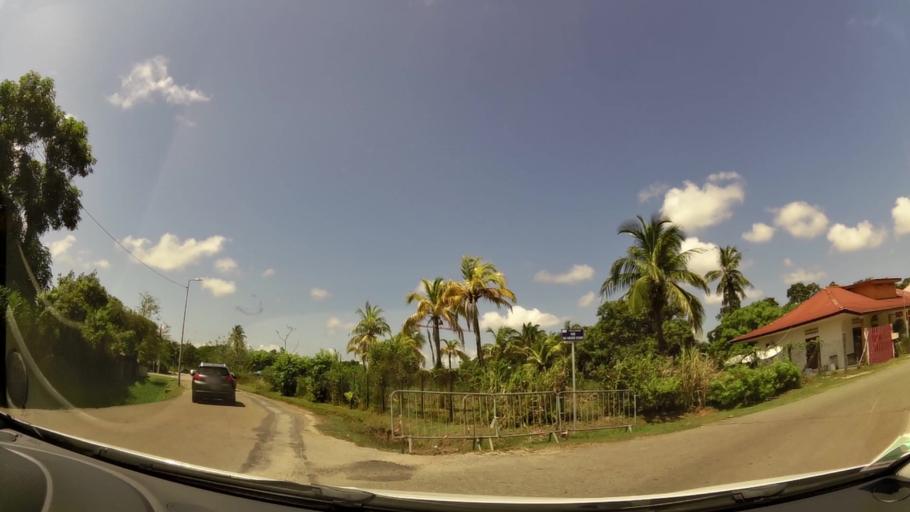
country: GF
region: Guyane
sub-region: Guyane
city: Cayenne
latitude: 4.9178
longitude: -52.3180
